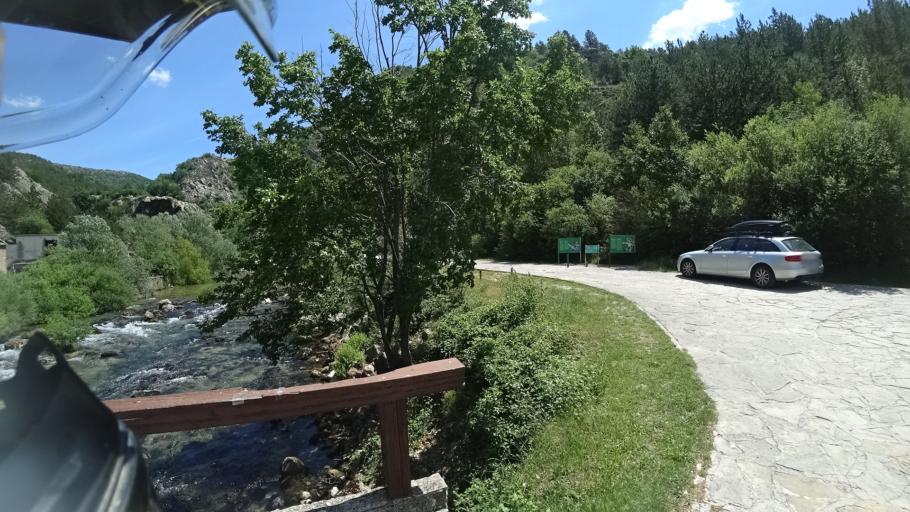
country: HR
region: Sibensko-Kniniska
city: Knin
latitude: 44.0411
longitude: 16.2328
